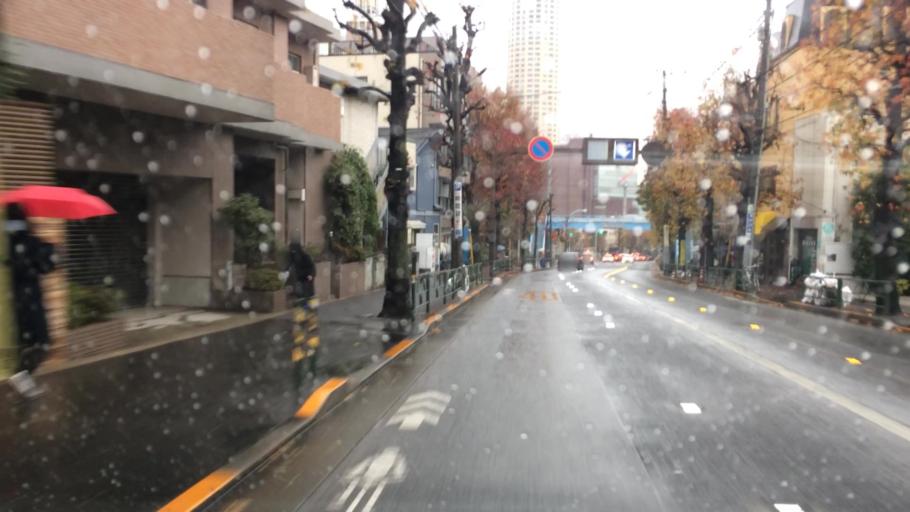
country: JP
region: Tokyo
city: Tokyo
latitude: 35.6390
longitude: 139.6980
